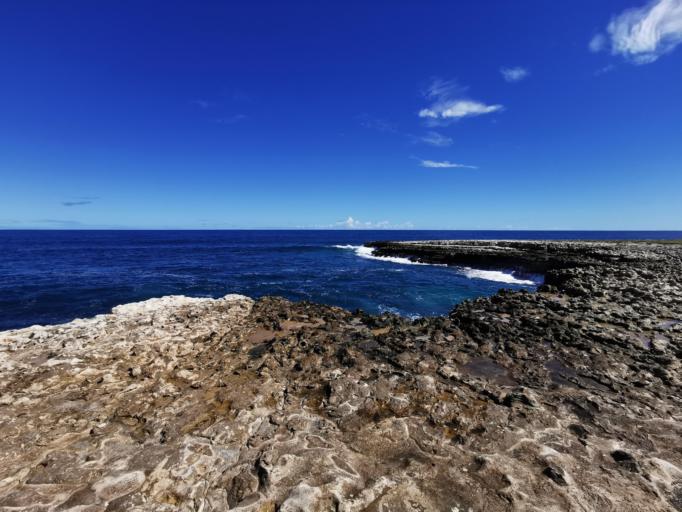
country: AG
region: Saint Peter
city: Parham
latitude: 17.1020
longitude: -61.6786
